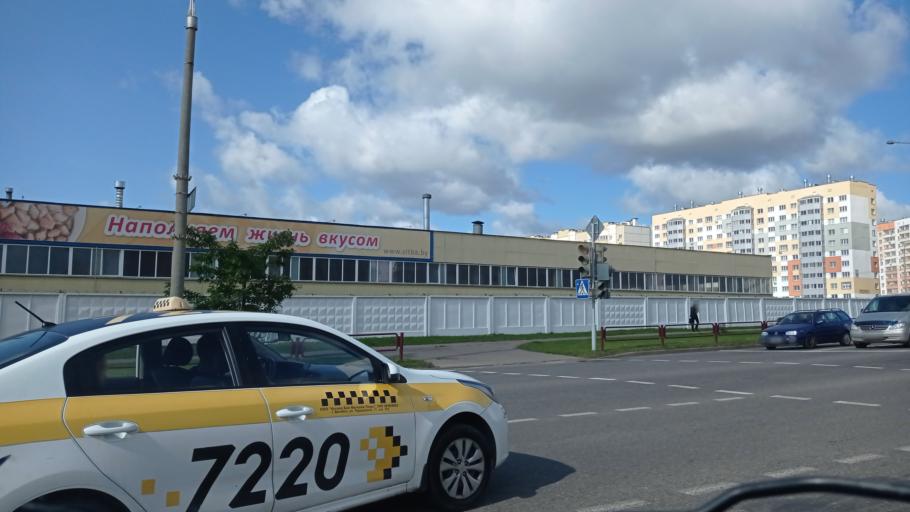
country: BY
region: Vitebsk
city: Vitebsk
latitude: 55.1704
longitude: 30.2572
